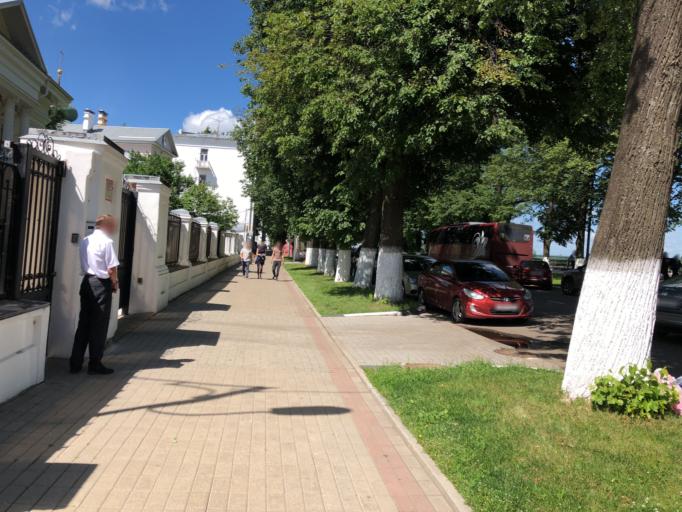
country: RU
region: Jaroslavl
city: Yaroslavl
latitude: 57.6299
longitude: 39.8957
